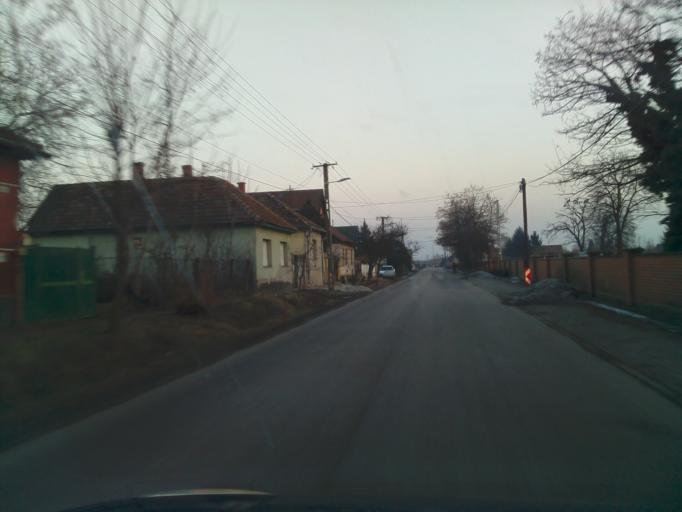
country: HU
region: Heves
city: Hatvan
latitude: 47.6695
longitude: 19.7047
